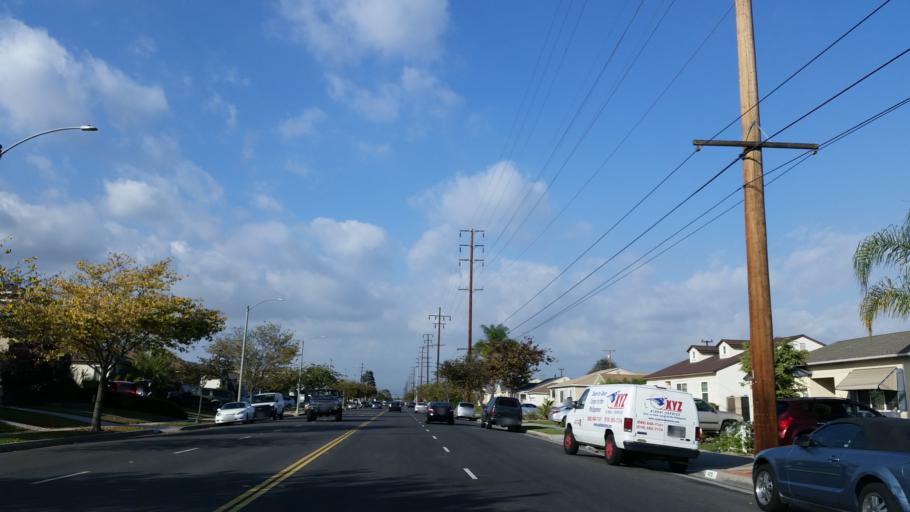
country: US
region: California
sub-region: Los Angeles County
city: Lakewood
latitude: 33.8363
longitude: -118.1077
